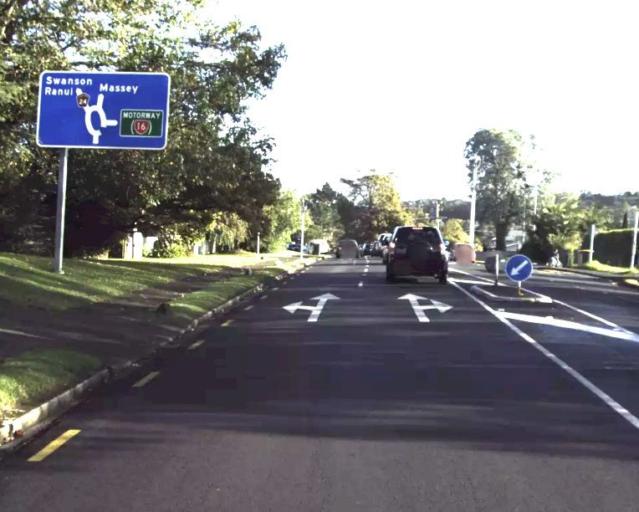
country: NZ
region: Auckland
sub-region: Auckland
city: Rosebank
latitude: -36.8617
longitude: 174.6129
